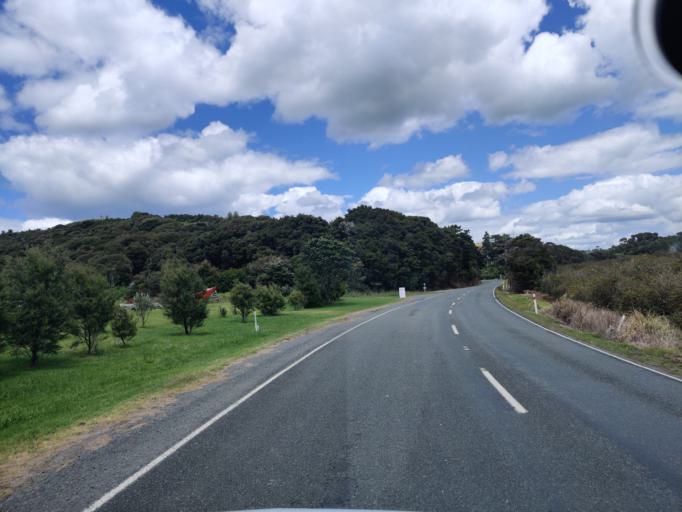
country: NZ
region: Northland
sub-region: Far North District
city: Paihia
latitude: -35.2744
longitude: 174.1398
